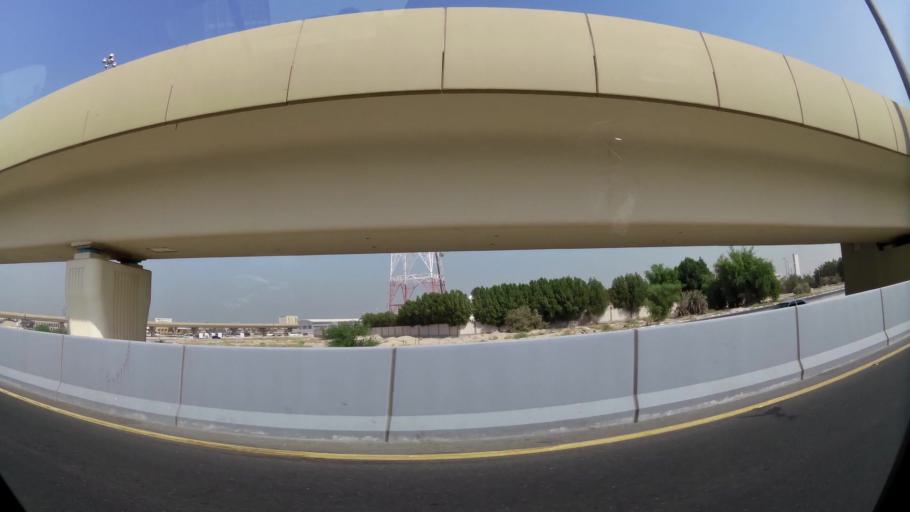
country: KW
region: Al Asimah
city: Ar Rabiyah
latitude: 29.3085
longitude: 47.8904
